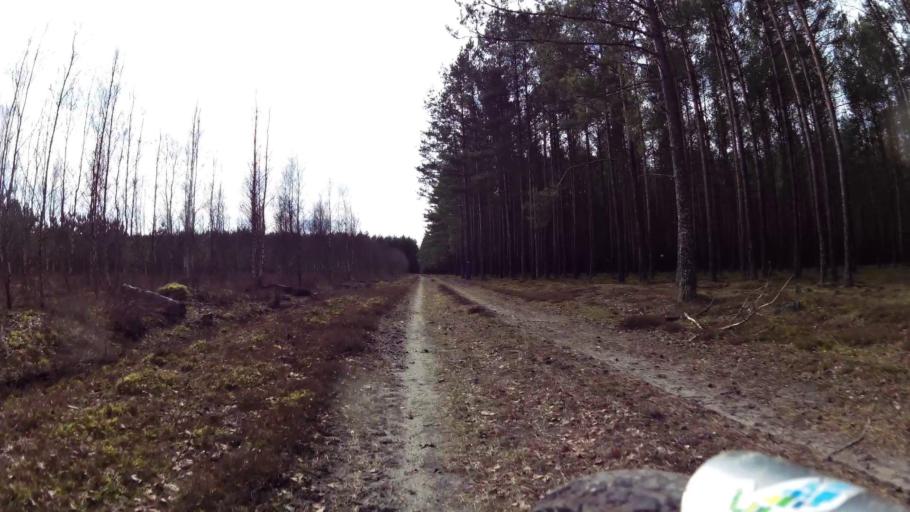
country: PL
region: Pomeranian Voivodeship
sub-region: Powiat bytowski
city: Kolczyglowy
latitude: 54.1897
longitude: 17.2135
